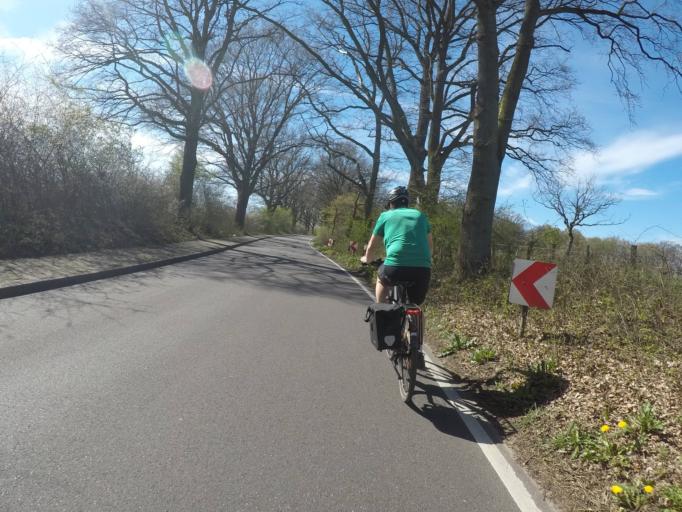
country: DE
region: Hamburg
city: Duvenstedt
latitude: 53.7111
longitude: 10.0887
